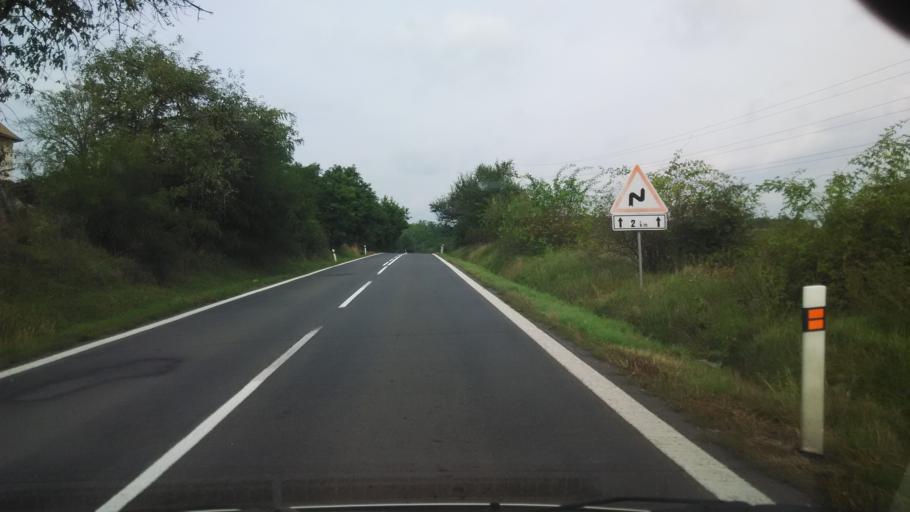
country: SK
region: Banskobystricky
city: Krupina
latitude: 48.3092
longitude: 19.0285
